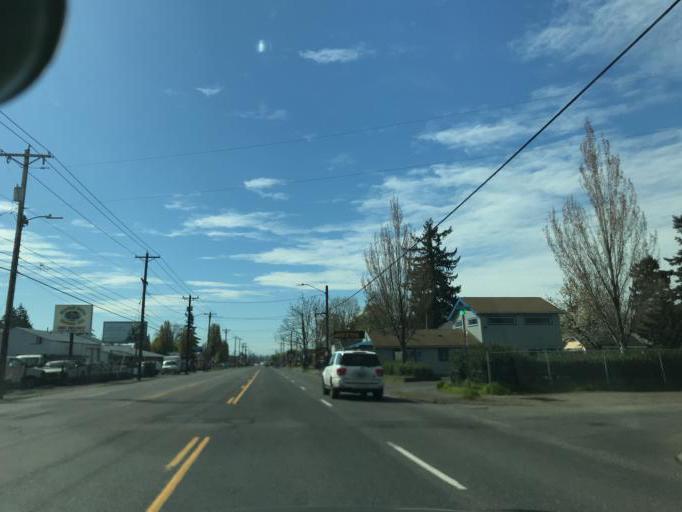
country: US
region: Oregon
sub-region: Multnomah County
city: Lents
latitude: 45.4722
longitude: -122.5791
